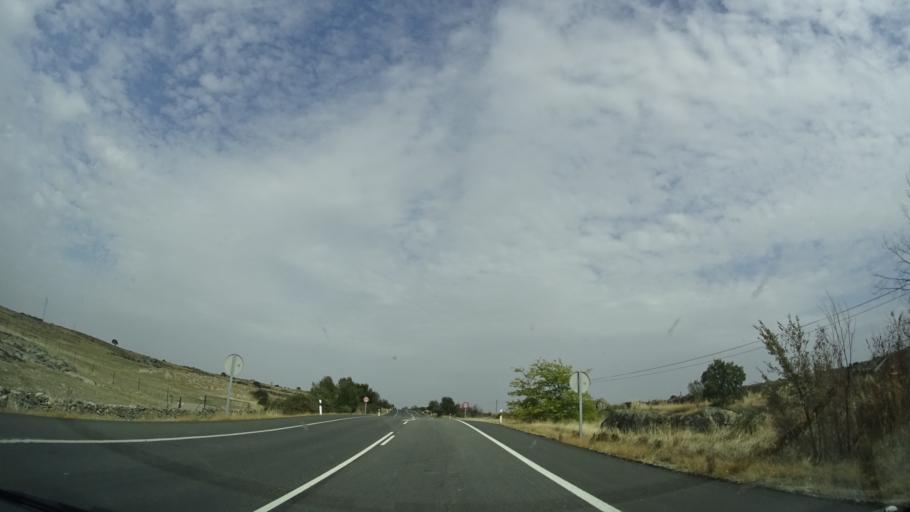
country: ES
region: Extremadura
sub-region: Provincia de Caceres
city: Trujillo
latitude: 39.4413
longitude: -5.8862
